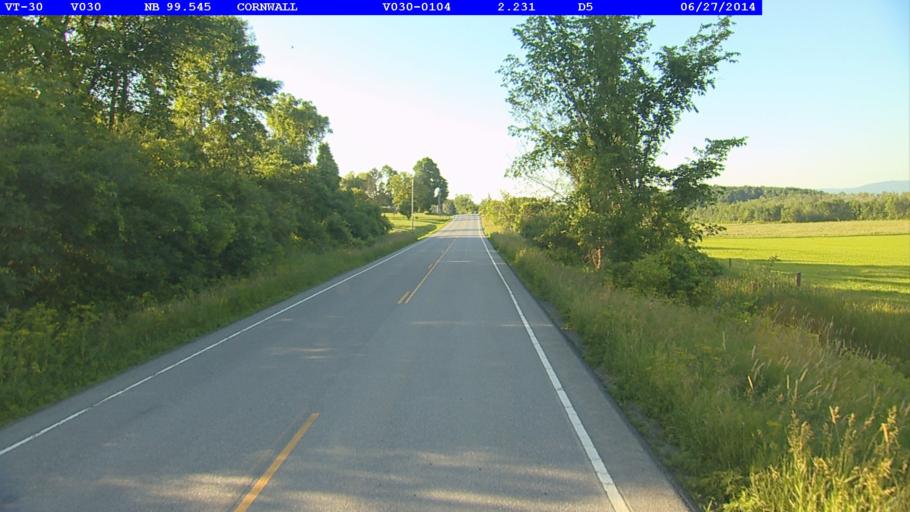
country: US
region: Vermont
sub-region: Addison County
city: Middlebury (village)
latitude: 43.9399
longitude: -73.2120
